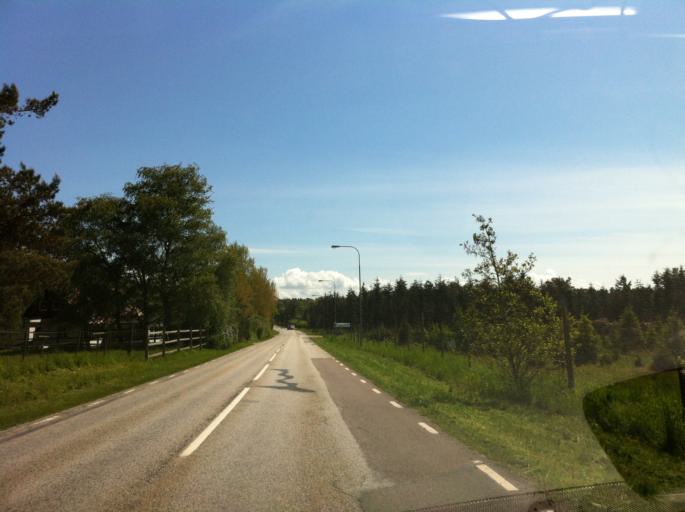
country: SE
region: Skane
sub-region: Kavlinge Kommun
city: Hofterup
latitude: 55.8220
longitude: 12.9695
